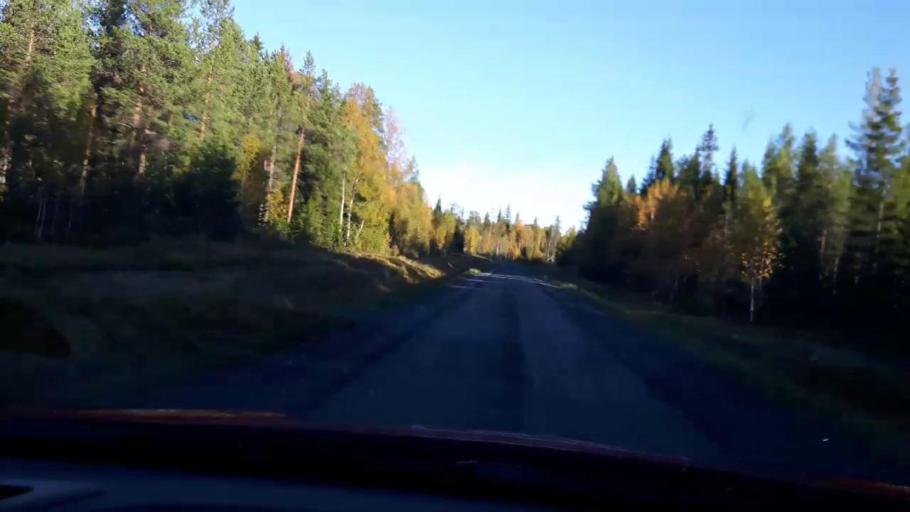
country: SE
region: Jaemtland
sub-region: OEstersunds Kommun
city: Lit
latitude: 63.5952
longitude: 14.8320
